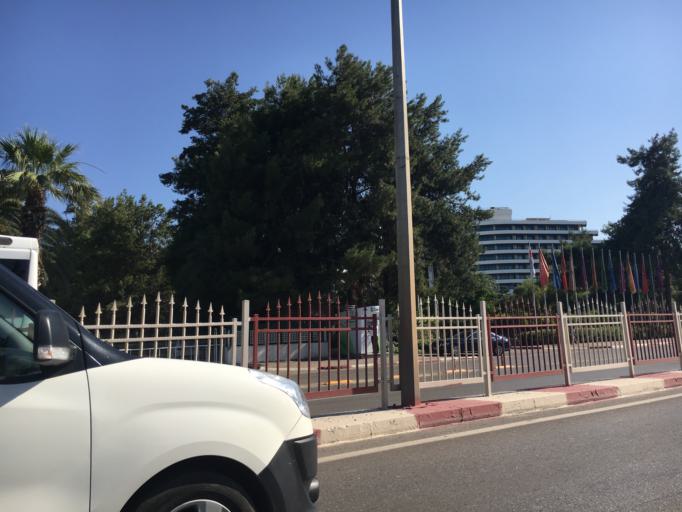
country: TR
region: Antalya
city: Antalya
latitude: 36.8875
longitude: 30.6755
